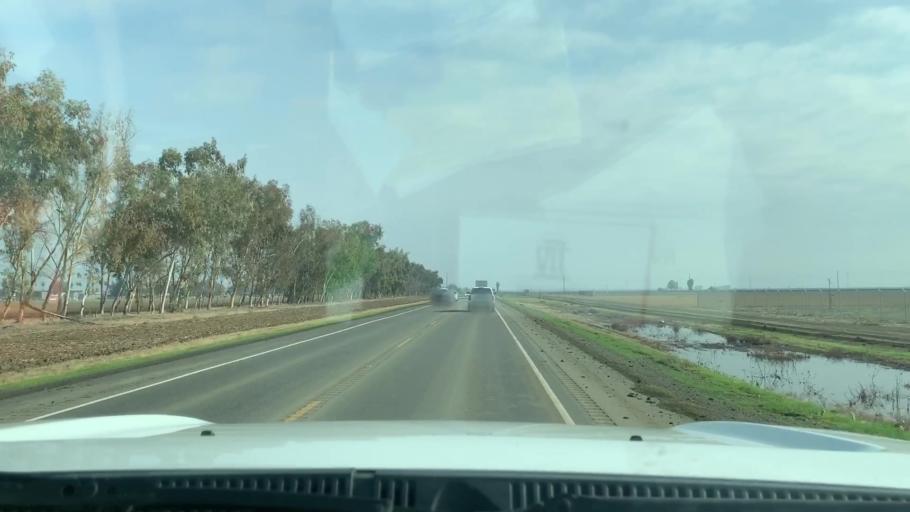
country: US
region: California
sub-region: Kings County
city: Lemoore Station
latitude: 36.2552
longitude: -119.9136
